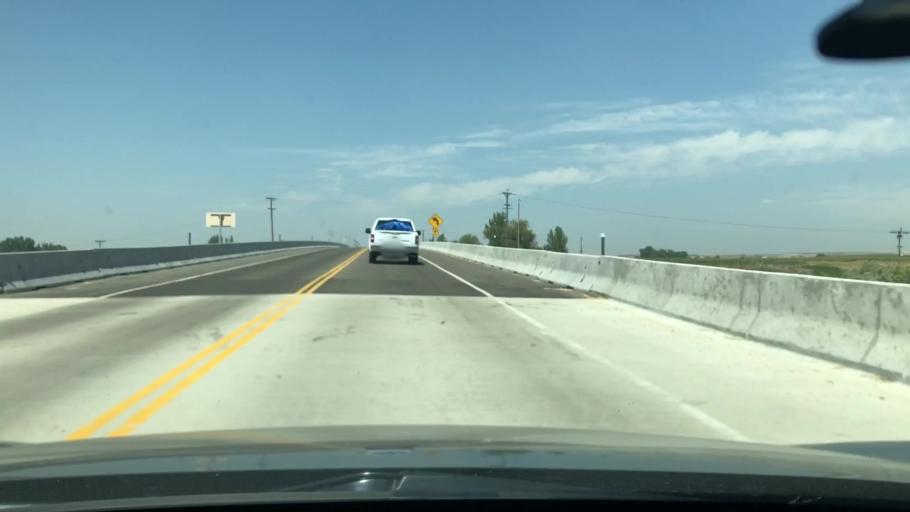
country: US
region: Idaho
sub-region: Canyon County
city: Parma
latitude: 43.7642
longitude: -116.9117
